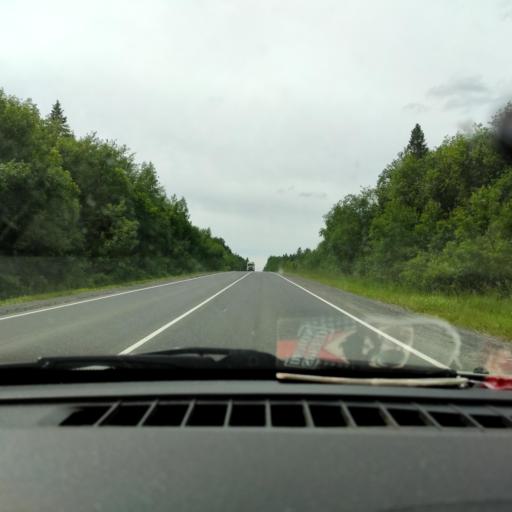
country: RU
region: Perm
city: Chusovoy
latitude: 58.3713
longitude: 58.0215
